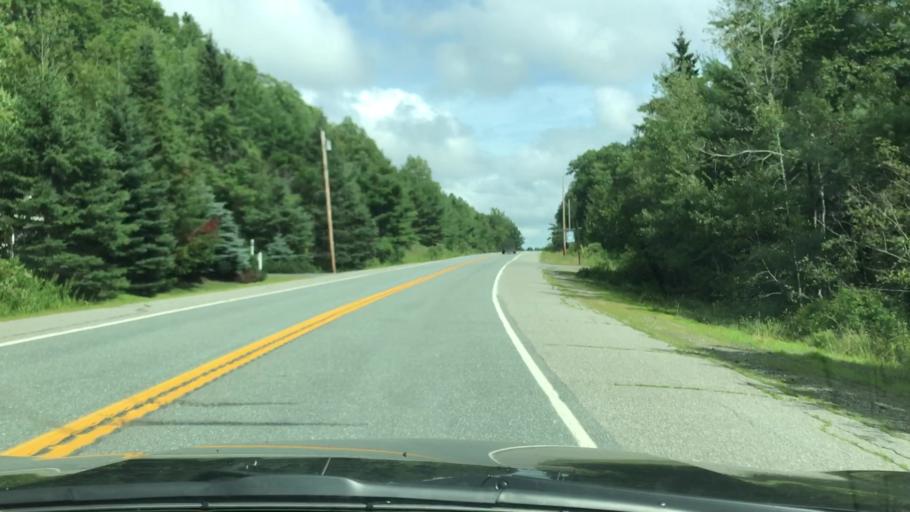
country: US
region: Maine
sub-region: Hancock County
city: Orland
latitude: 44.5672
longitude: -68.6735
